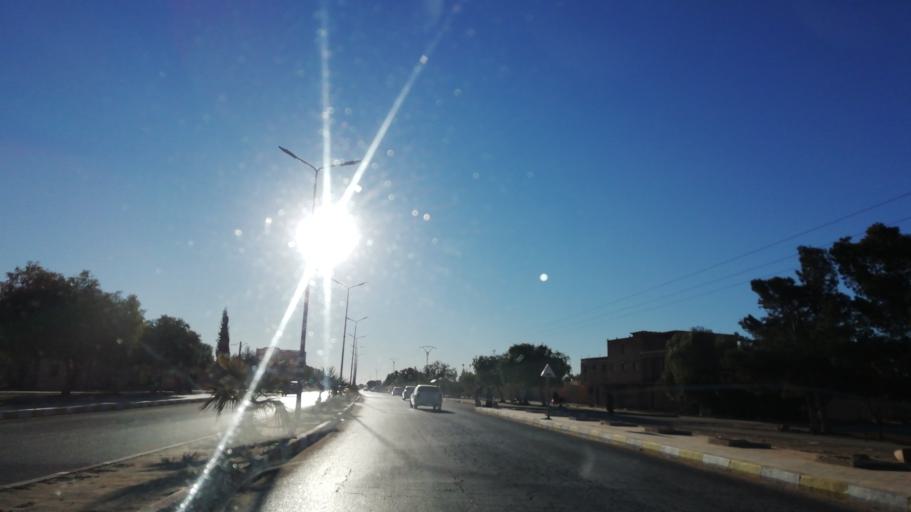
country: DZ
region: Saida
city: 'Ain el Hadjar
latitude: 34.0315
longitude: 0.0896
